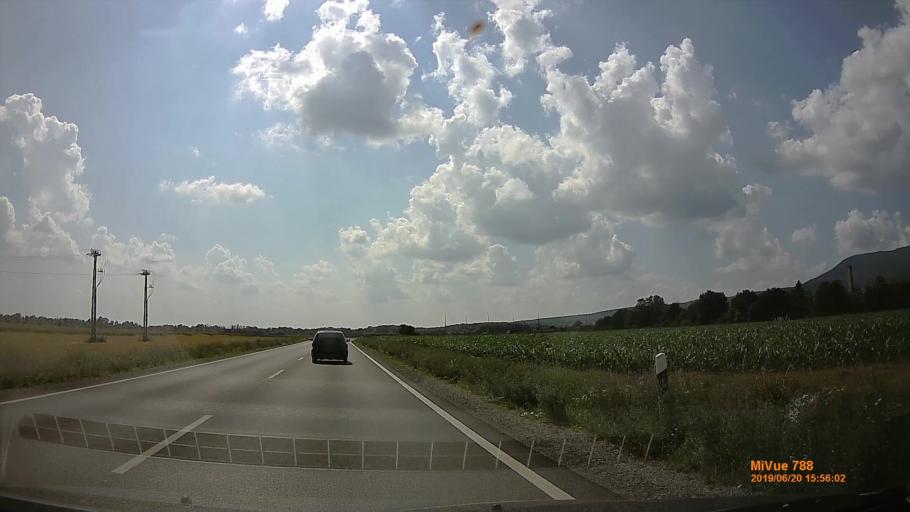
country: HU
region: Baranya
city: Pellerd
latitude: 46.0550
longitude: 18.1811
